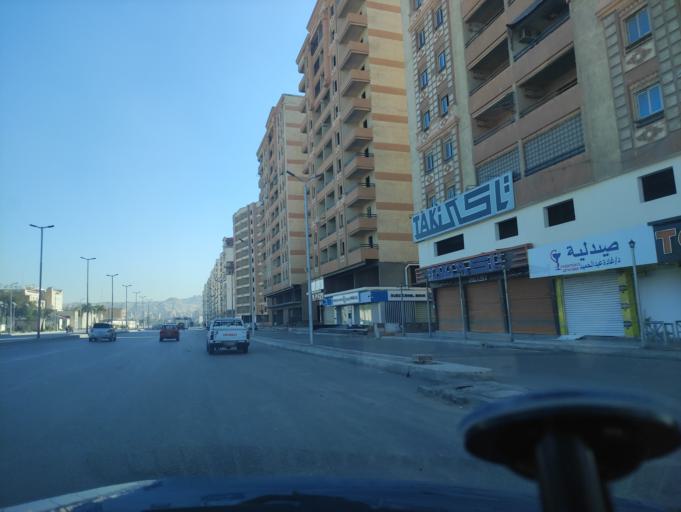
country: EG
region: Al Jizah
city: Al Jizah
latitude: 30.0032
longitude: 31.2430
